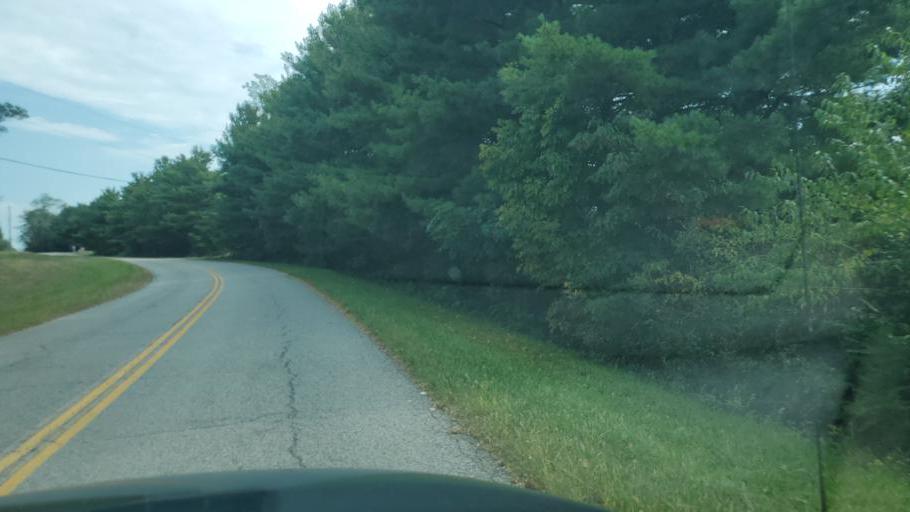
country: US
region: Ohio
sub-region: Muskingum County
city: Zanesville
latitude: 39.9446
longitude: -82.1376
